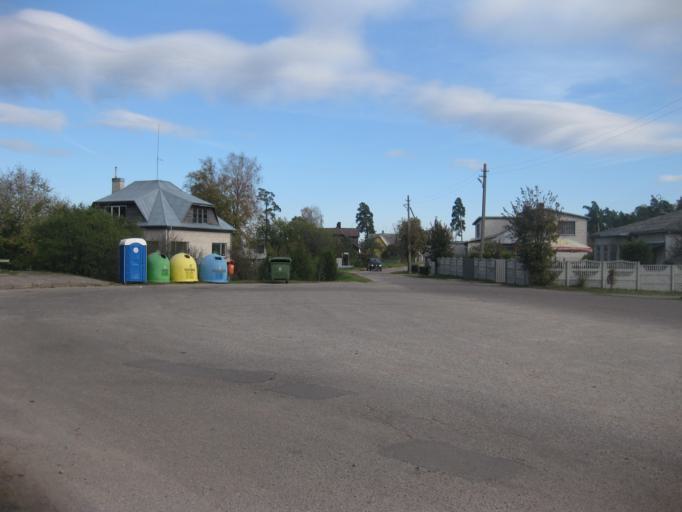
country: LT
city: Ezerelis
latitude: 54.8808
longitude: 23.6130
